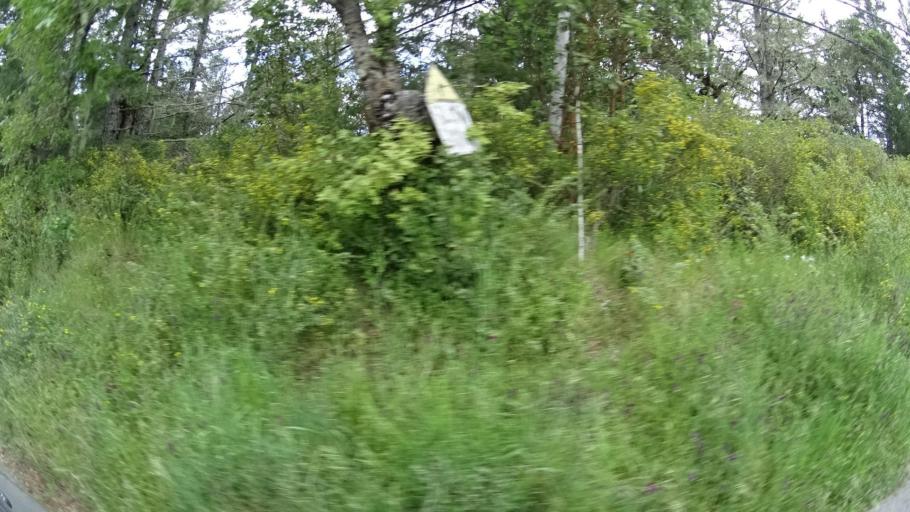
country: US
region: California
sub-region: Humboldt County
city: Redway
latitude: 40.1100
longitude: -123.7785
